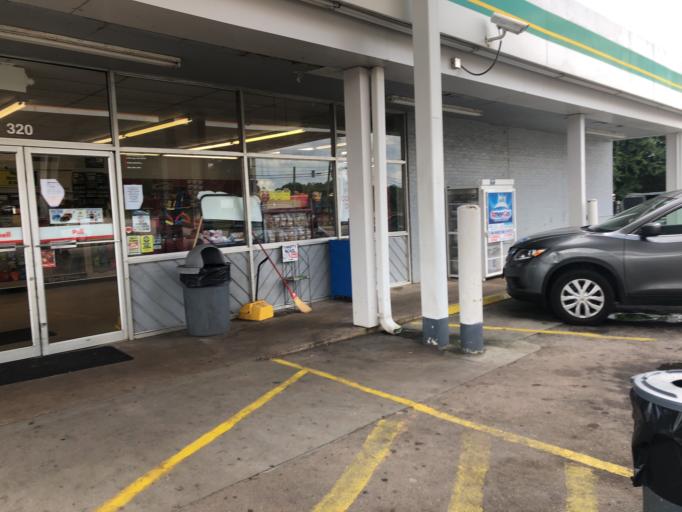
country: US
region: Georgia
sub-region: Troup County
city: La Grange
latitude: 33.0476
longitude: -85.0143
